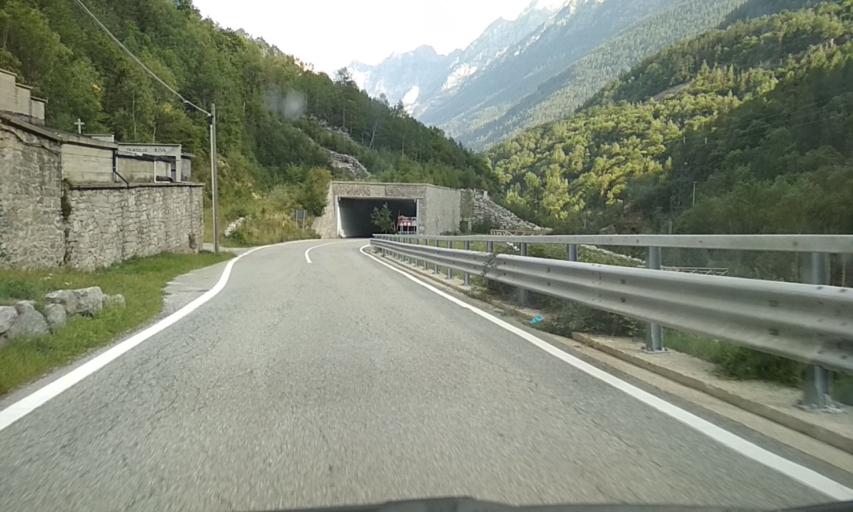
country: IT
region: Piedmont
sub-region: Provincia di Torino
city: Noasca
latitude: 45.4506
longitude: 7.3201
